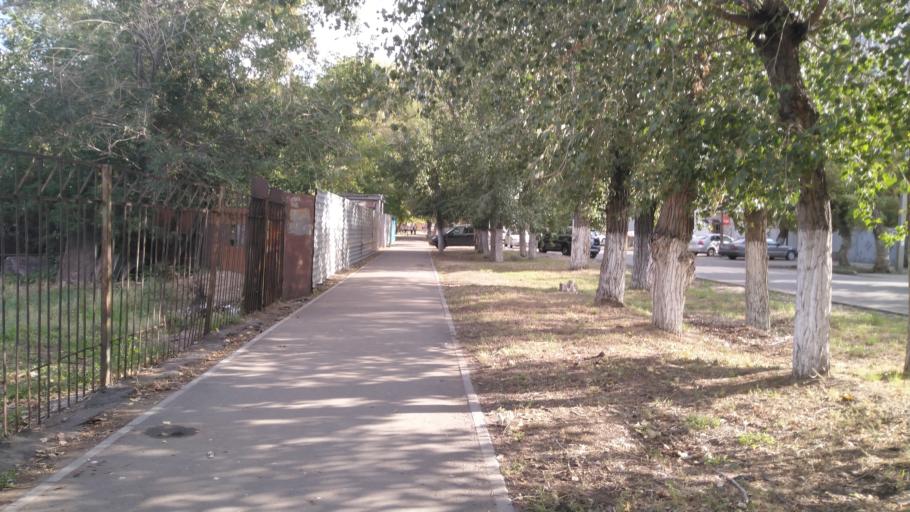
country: KZ
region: Pavlodar
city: Pavlodar
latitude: 52.2765
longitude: 76.9466
